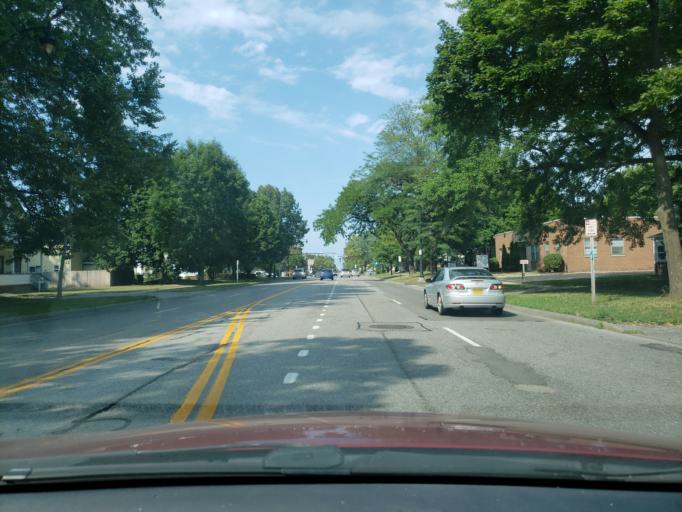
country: US
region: New York
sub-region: Monroe County
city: Irondequoit
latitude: 43.2484
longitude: -77.6157
